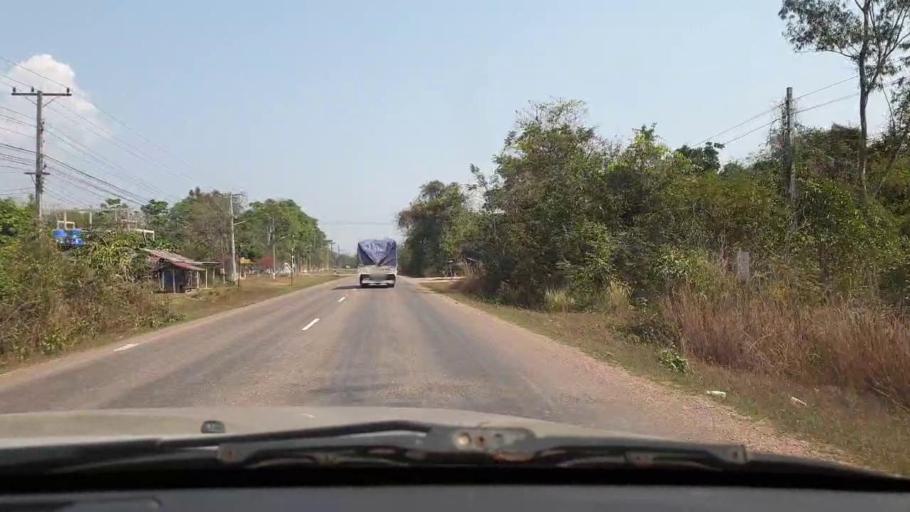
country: TH
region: Nong Khai
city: Phon Phisai
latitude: 18.1511
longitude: 103.0557
